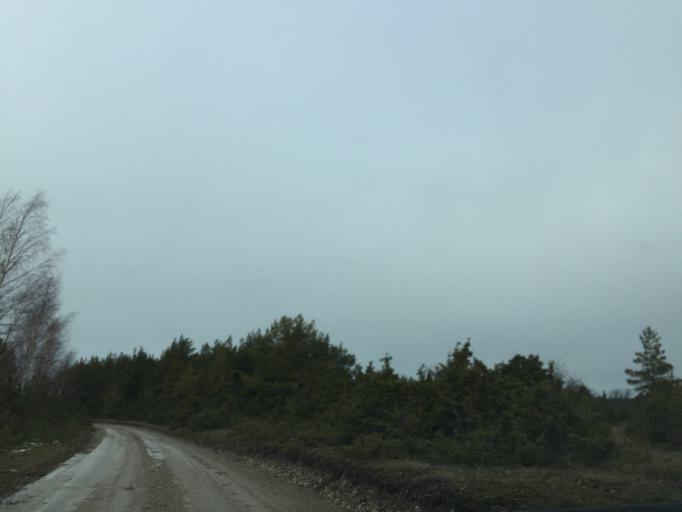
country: EE
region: Saare
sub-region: Kuressaare linn
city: Kuressaare
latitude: 58.4994
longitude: 21.9232
